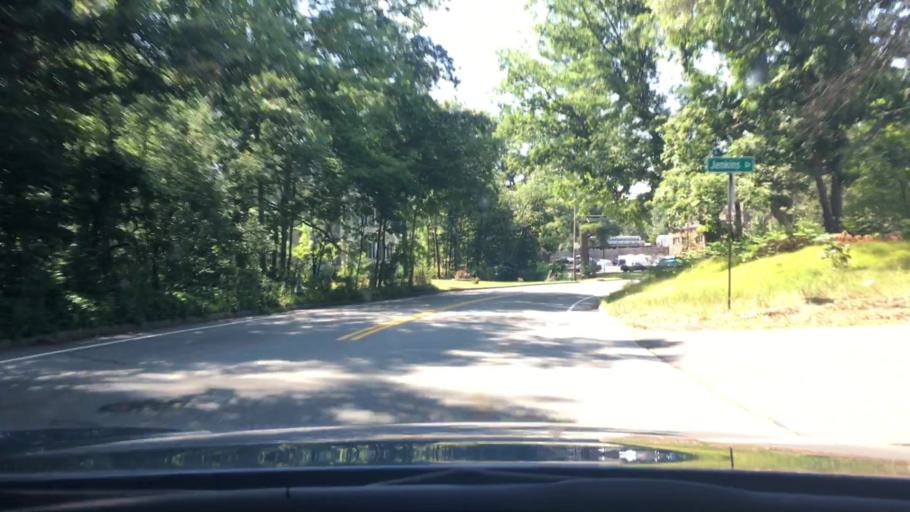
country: US
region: Massachusetts
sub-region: Middlesex County
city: Billerica
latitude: 42.5746
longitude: -71.2895
